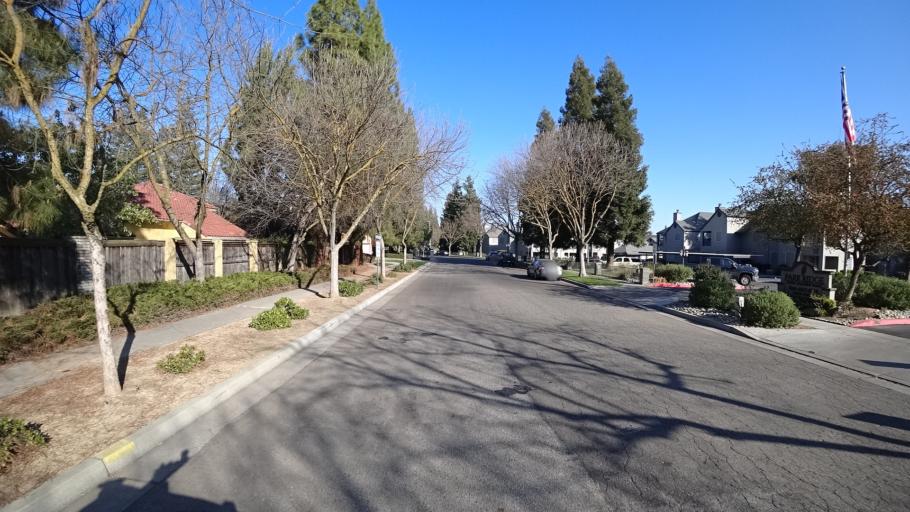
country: US
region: California
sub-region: Fresno County
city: Clovis
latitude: 36.8623
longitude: -119.7937
